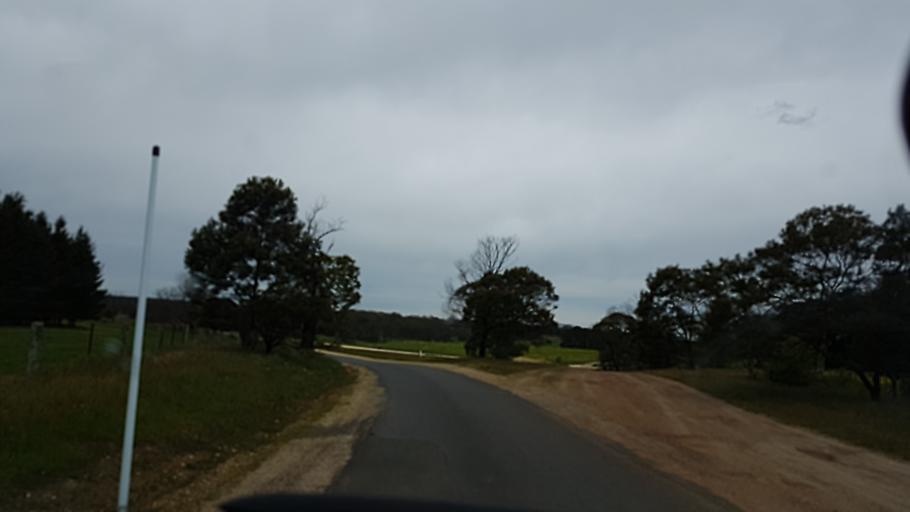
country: AU
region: Victoria
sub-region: Moorabool
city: Bacchus Marsh
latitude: -37.7843
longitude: 144.1431
